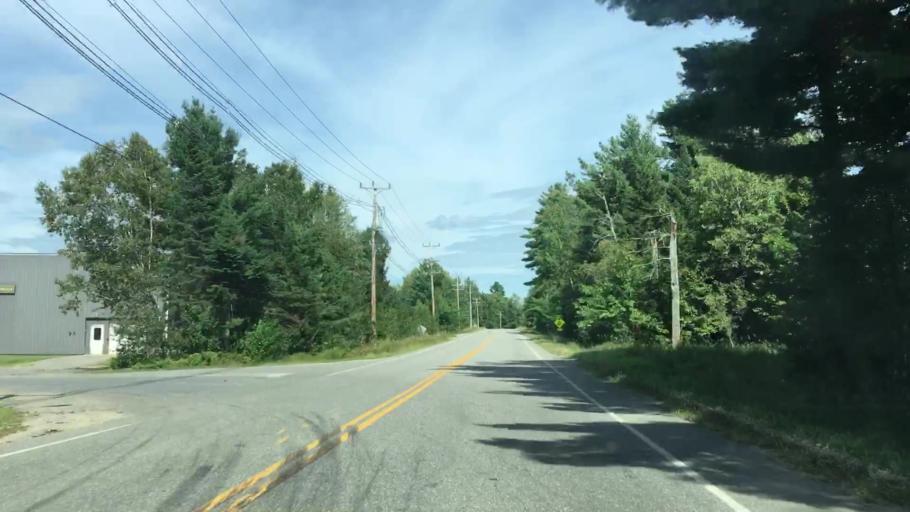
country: US
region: Maine
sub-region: Penobscot County
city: Lincoln
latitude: 45.3907
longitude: -68.5323
